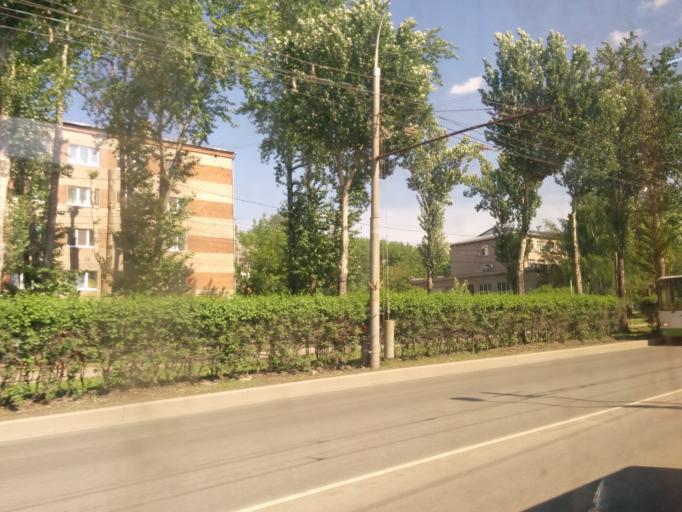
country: RU
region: Perm
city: Perm
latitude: 58.0099
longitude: 56.2814
